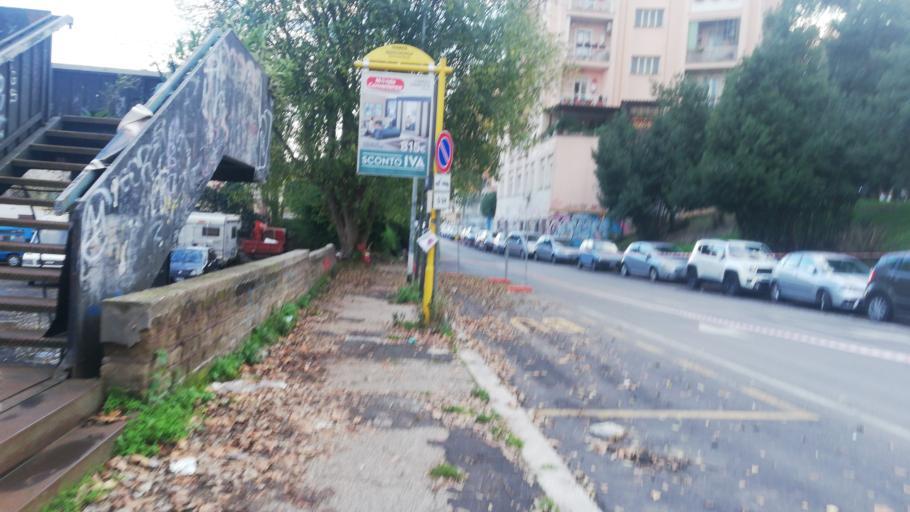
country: IT
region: Latium
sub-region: Citta metropolitana di Roma Capitale
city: Rome
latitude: 41.9328
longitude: 12.5291
